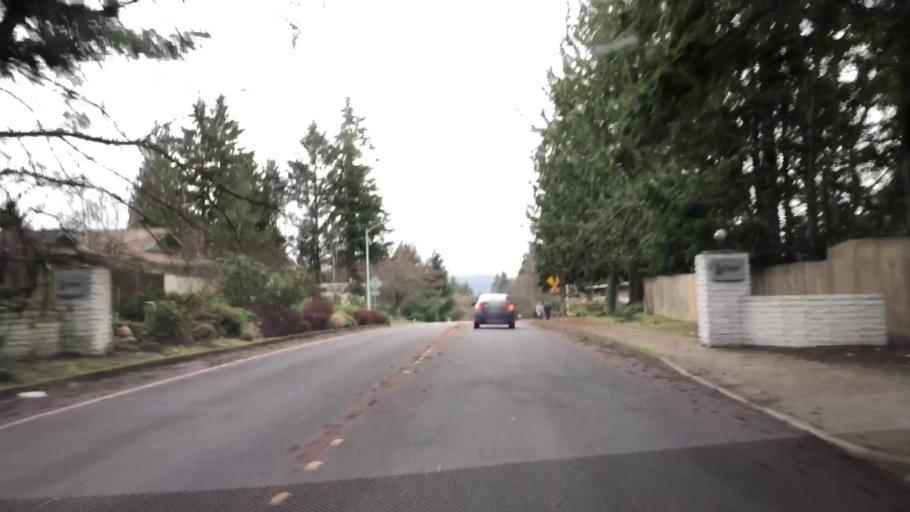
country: US
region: Washington
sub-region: King County
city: West Lake Sammamish
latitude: 47.6169
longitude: -122.1167
